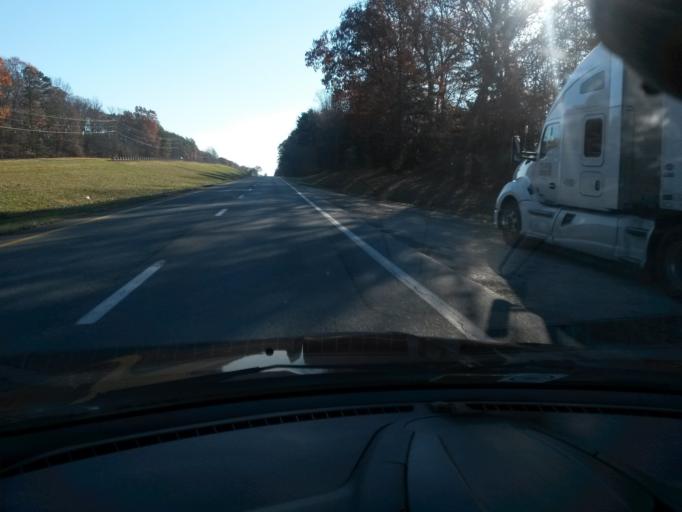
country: US
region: Virginia
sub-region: Appomattox County
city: Appomattox
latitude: 37.2855
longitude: -78.7200
